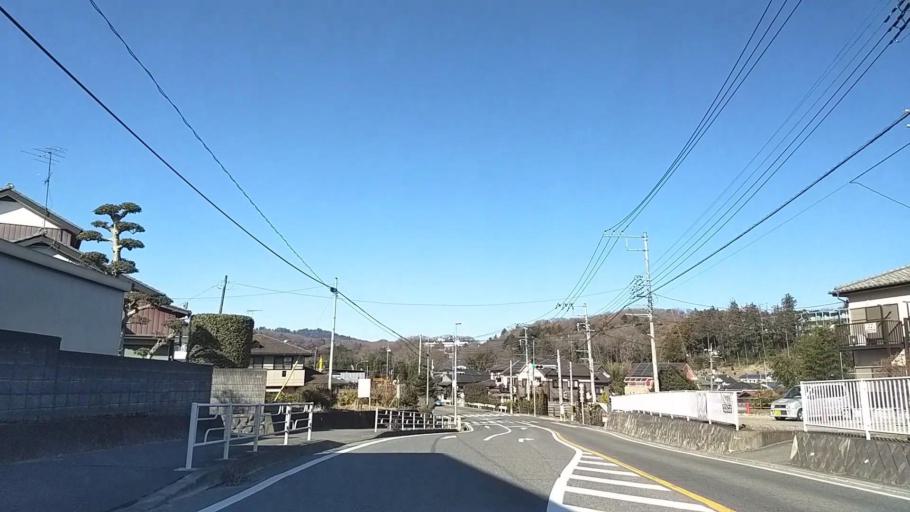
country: JP
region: Tokyo
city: Hachioji
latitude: 35.6090
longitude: 139.2951
